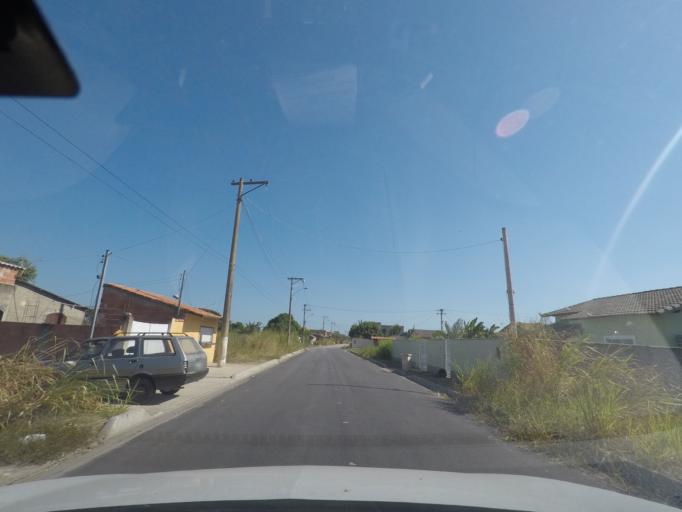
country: BR
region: Rio de Janeiro
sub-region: Marica
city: Marica
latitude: -22.9586
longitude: -42.9246
